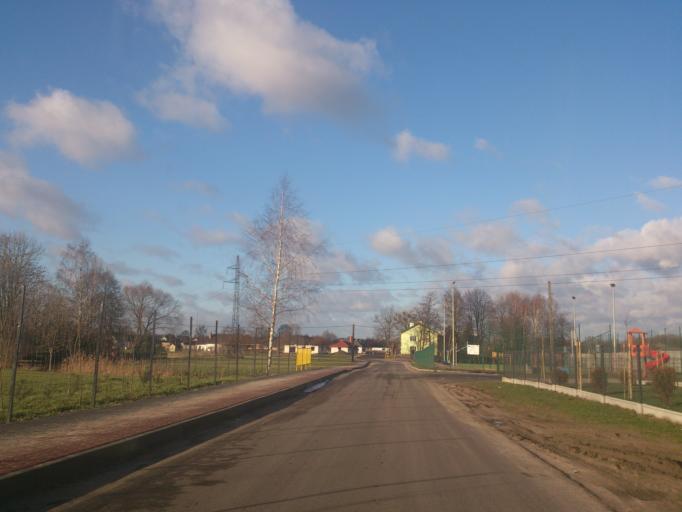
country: PL
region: Kujawsko-Pomorskie
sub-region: Powiat torunski
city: Lubicz Gorny
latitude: 53.0238
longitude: 18.8044
